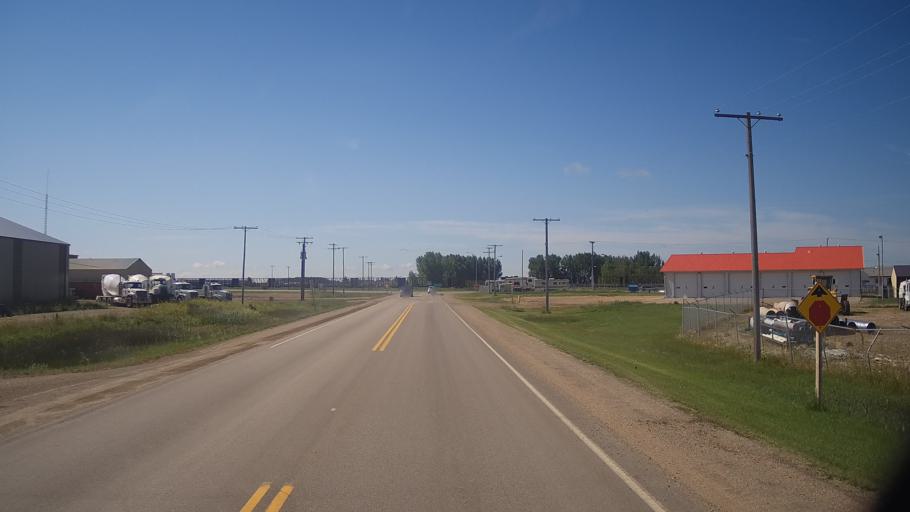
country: CA
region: Saskatchewan
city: Watrous
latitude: 51.6680
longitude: -105.4516
